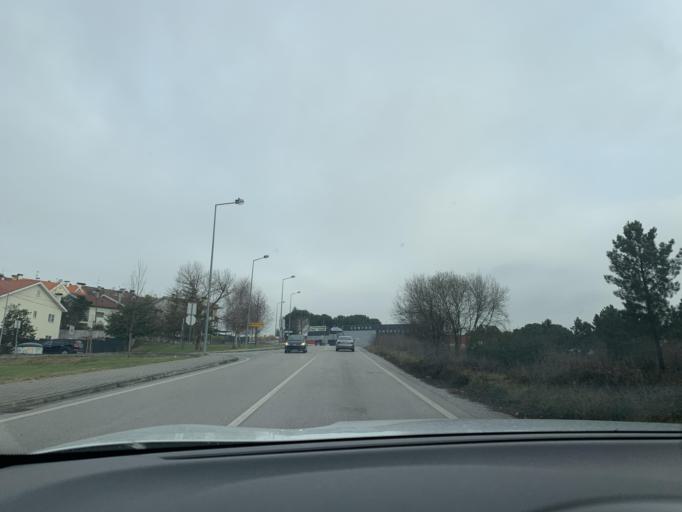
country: PT
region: Viseu
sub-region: Viseu
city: Viseu
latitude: 40.6313
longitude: -7.9037
